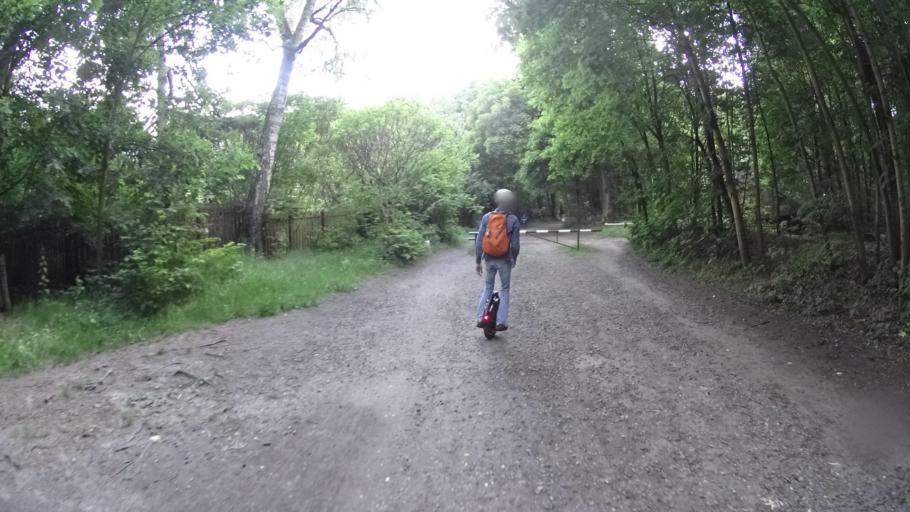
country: PL
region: Masovian Voivodeship
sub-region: Warszawa
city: Kabaty
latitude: 52.1186
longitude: 21.0861
